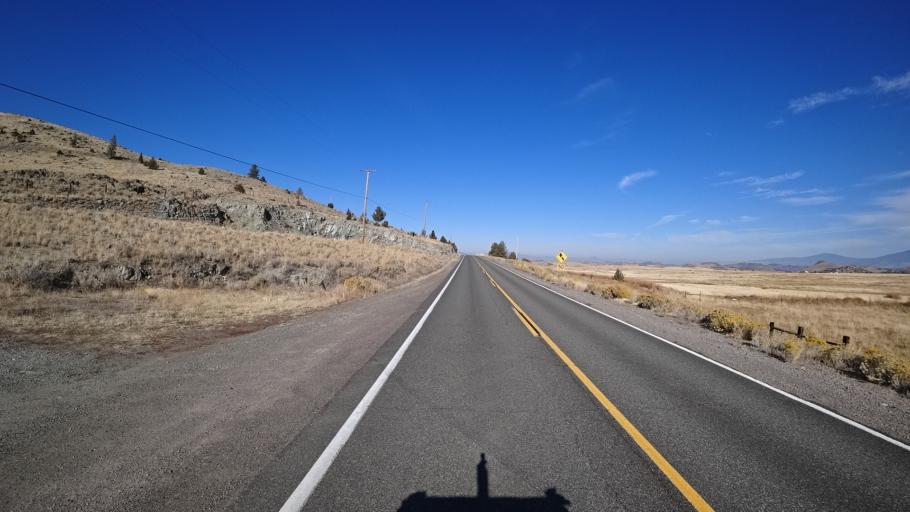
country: US
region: California
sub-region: Siskiyou County
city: Weed
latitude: 41.4644
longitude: -122.4652
